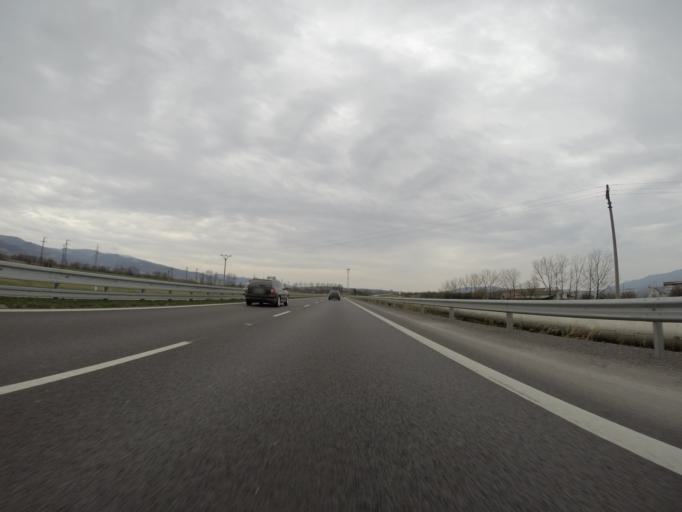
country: SK
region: Nitriansky
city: Prievidza
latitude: 48.7331
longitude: 18.6094
